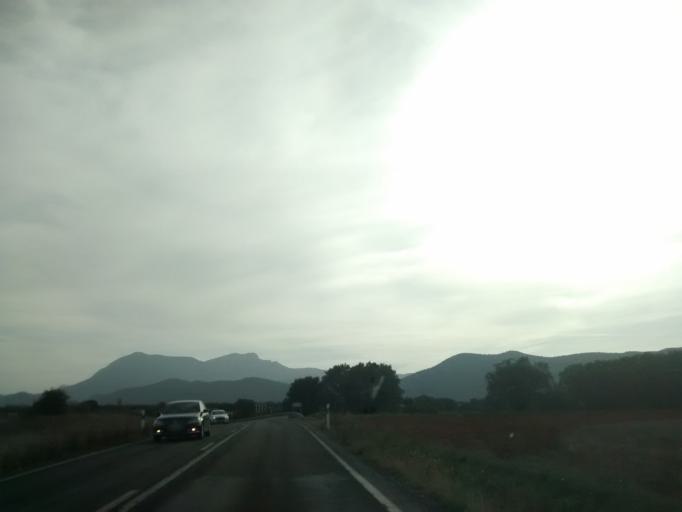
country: ES
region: Aragon
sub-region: Provincia de Huesca
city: Bailo
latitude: 42.5781
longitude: -0.8234
